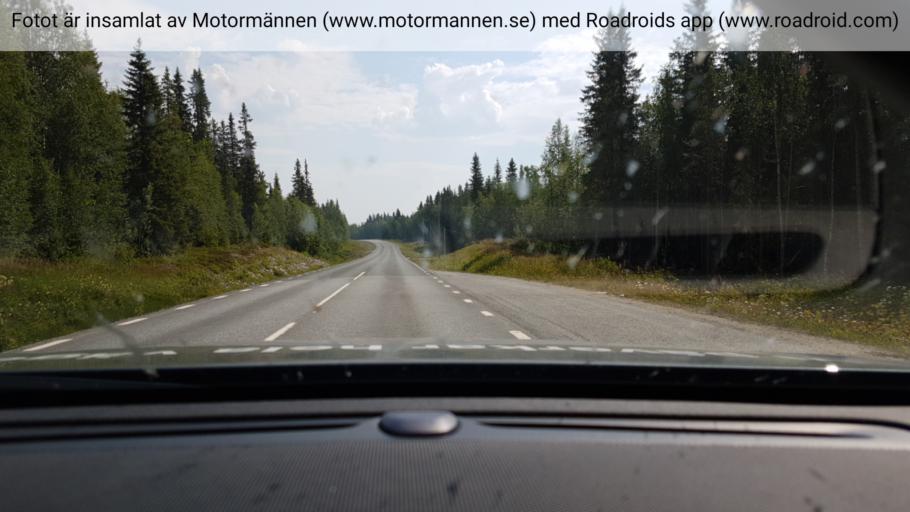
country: SE
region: Vaesterbotten
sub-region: Vilhelmina Kommun
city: Sjoberg
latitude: 65.4822
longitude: 15.8350
